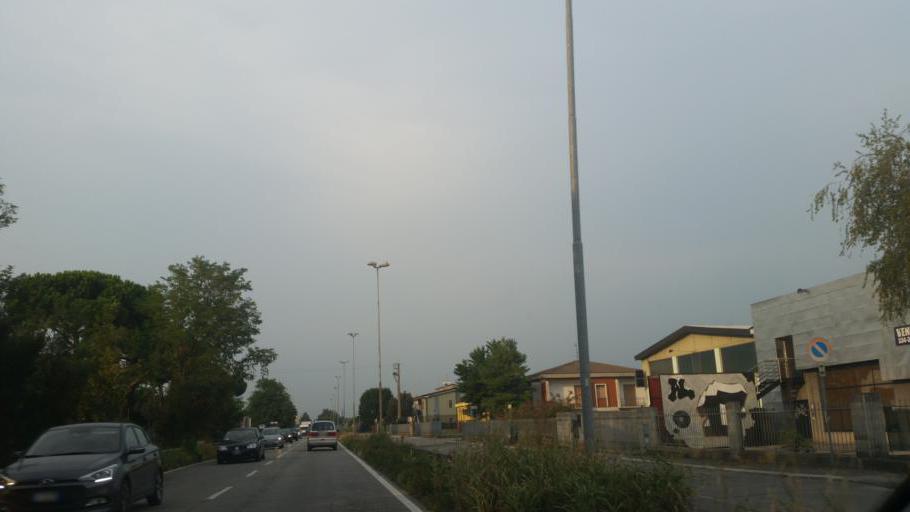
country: IT
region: Lombardy
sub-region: Provincia di Brescia
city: Barbariga
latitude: 45.3973
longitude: 10.0694
